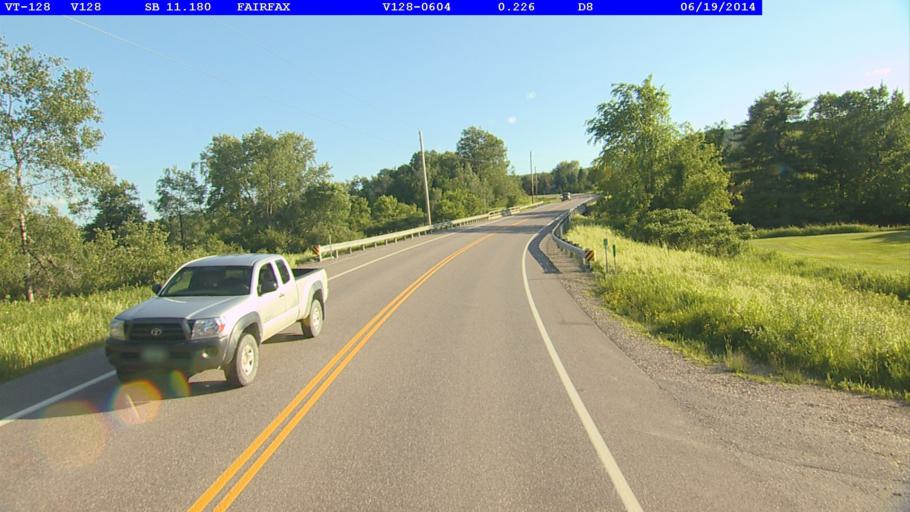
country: US
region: Vermont
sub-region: Chittenden County
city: Milton
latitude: 44.6500
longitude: -73.0120
